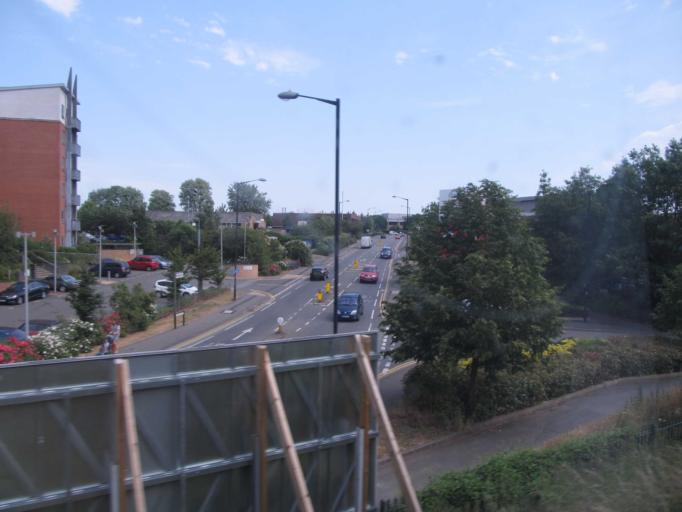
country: GB
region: England
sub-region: Buckinghamshire
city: Farnham Royal
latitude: 51.5229
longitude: -0.6424
